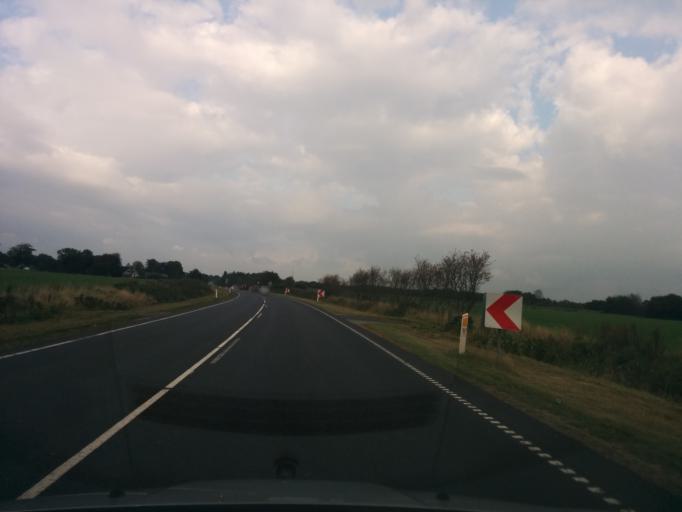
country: DK
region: South Denmark
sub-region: Billund Kommune
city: Grindsted
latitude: 55.6417
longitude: 8.8028
